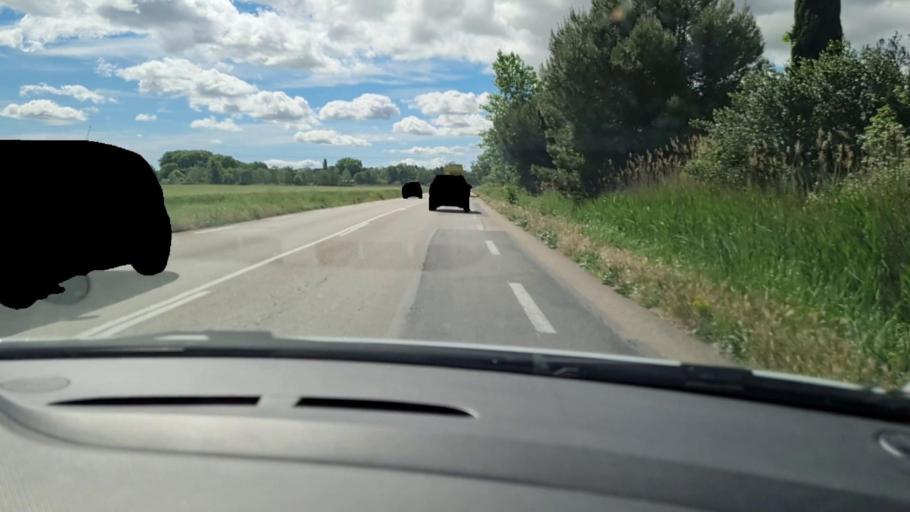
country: FR
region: Languedoc-Roussillon
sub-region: Departement du Gard
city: Caissargues
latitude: 43.7958
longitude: 4.3449
